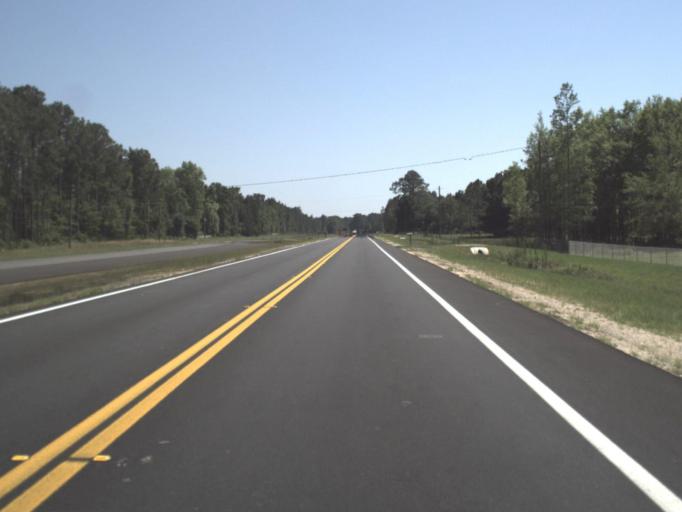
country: US
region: Florida
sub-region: Duval County
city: Baldwin
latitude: 30.3443
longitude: -81.9539
